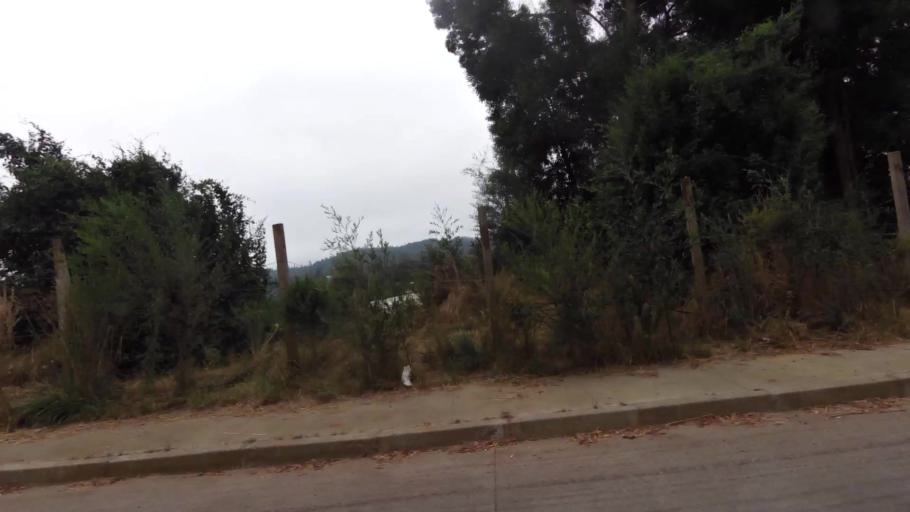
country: CL
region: Biobio
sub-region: Provincia de Concepcion
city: Concepcion
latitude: -36.8354
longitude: -72.9997
